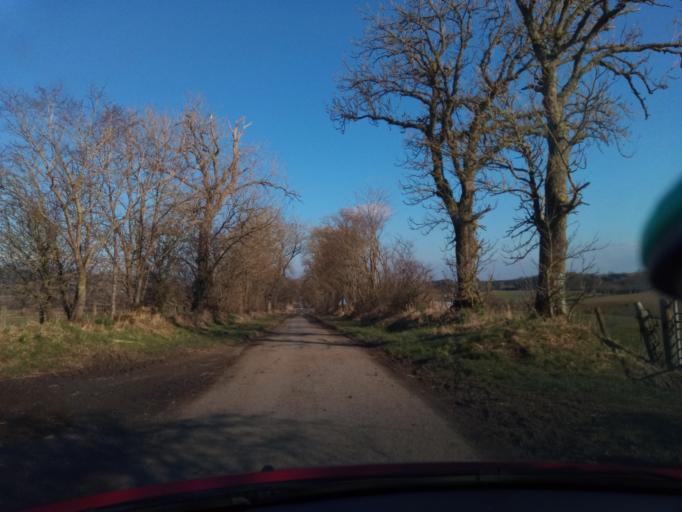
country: GB
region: Scotland
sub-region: The Scottish Borders
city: Hawick
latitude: 55.4997
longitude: -2.7729
